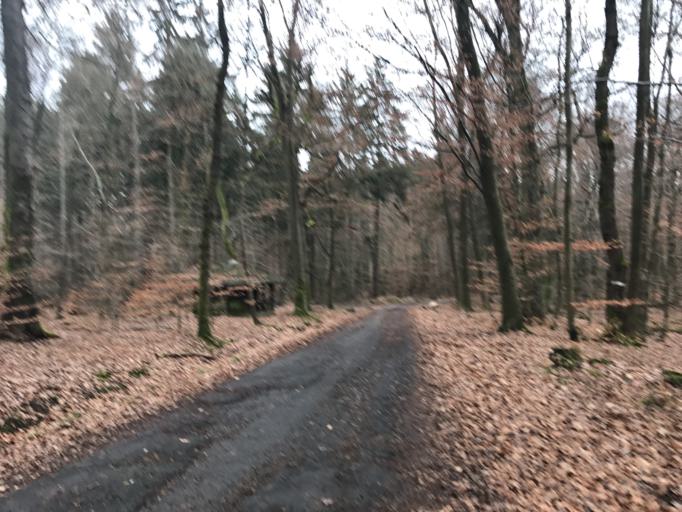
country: DE
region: Hesse
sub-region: Regierungsbezirk Darmstadt
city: Wiesbaden
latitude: 50.1217
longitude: 8.2389
